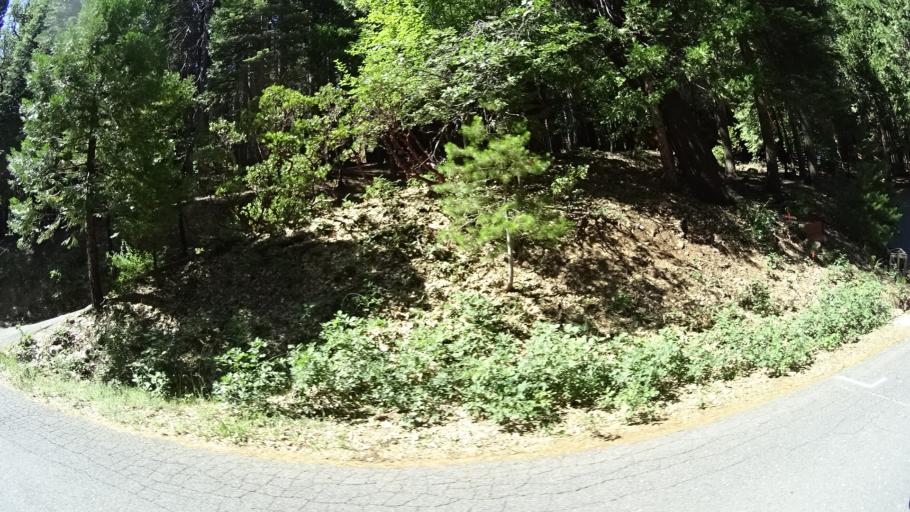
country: US
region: California
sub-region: Calaveras County
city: Arnold
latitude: 38.2886
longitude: -120.2832
